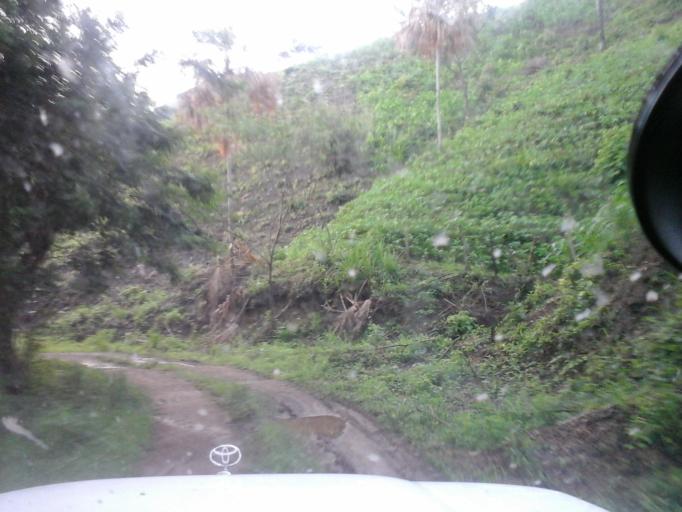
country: CO
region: Cesar
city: Agustin Codazzi
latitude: 10.1735
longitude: -73.1464
